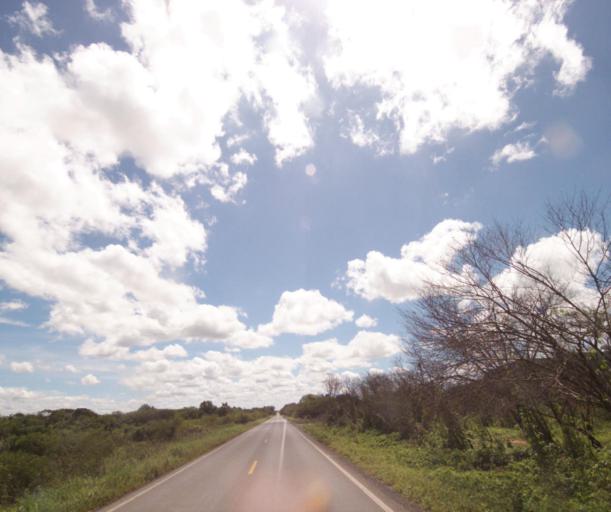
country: BR
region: Bahia
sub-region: Sao Felix Do Coribe
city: Santa Maria da Vitoria
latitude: -13.3935
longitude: -44.1259
